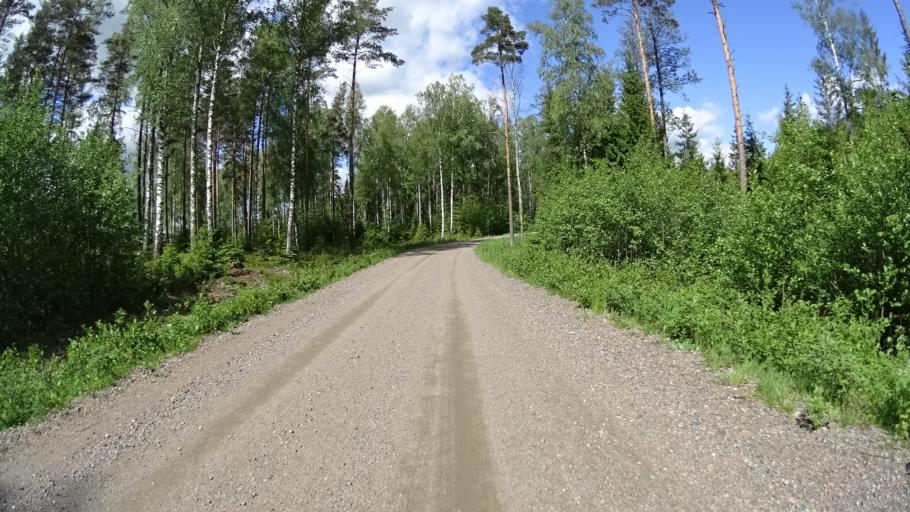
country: FI
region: Uusimaa
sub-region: Raaseporin
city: Karis
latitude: 60.1347
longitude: 23.6216
